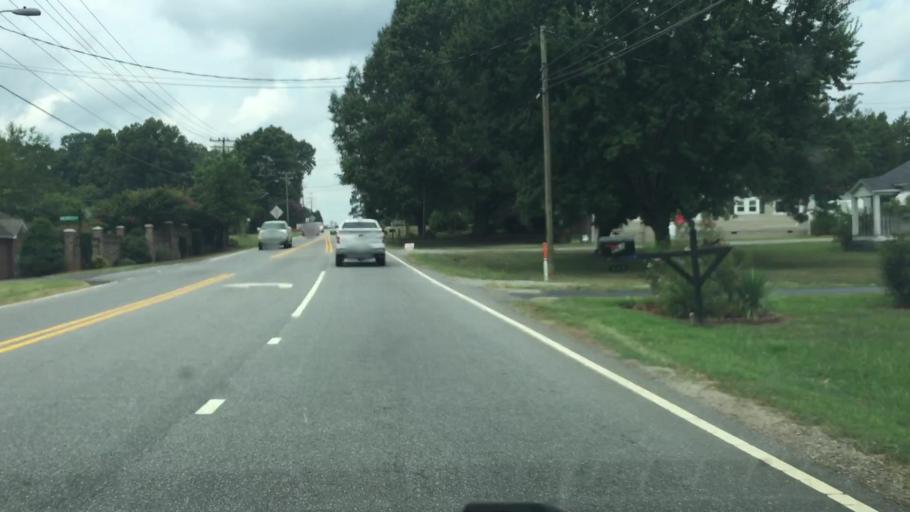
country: US
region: North Carolina
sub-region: Iredell County
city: Troutman
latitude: 35.6966
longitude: -80.8776
